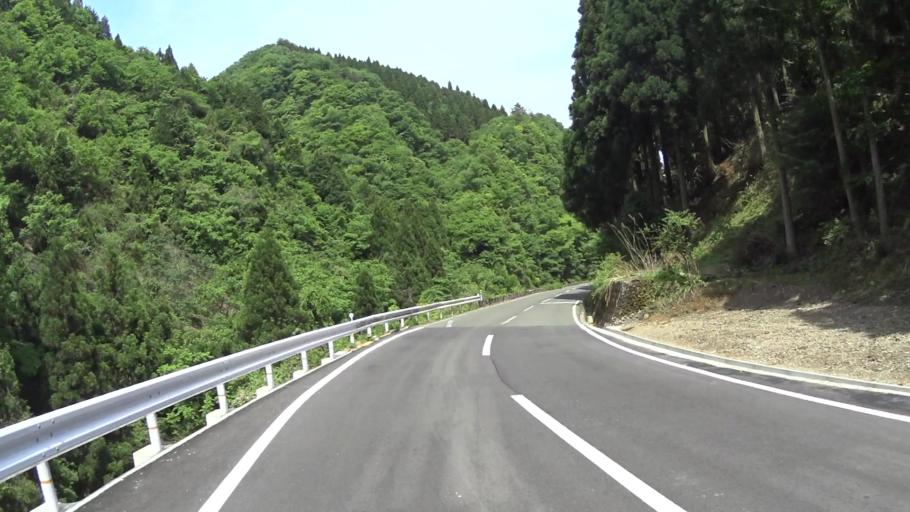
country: JP
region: Kyoto
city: Maizuru
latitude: 35.4419
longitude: 135.4934
